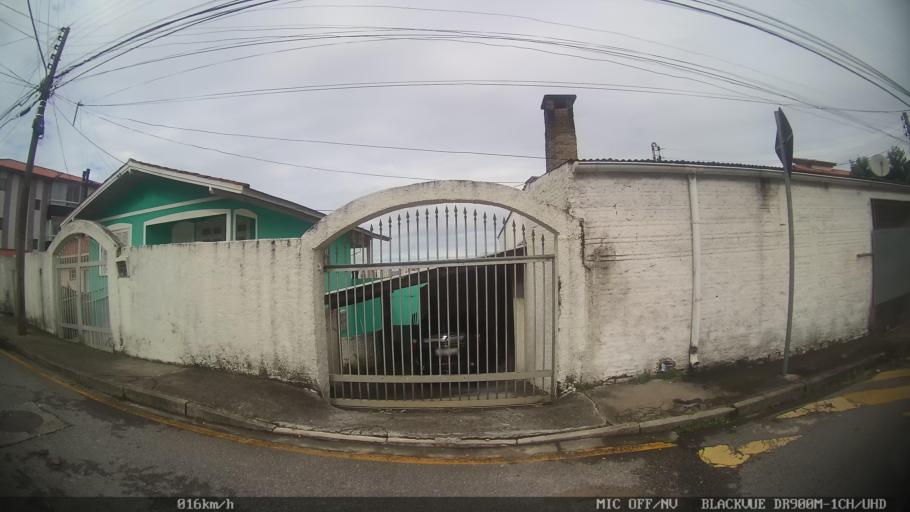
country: BR
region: Santa Catarina
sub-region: Sao Jose
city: Campinas
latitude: -27.5727
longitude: -48.6254
